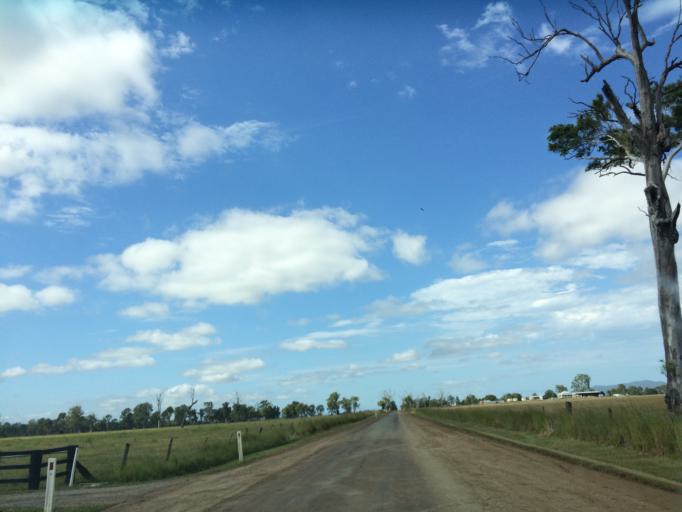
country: AU
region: Queensland
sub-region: Logan
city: Cedar Vale
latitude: -27.8730
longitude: 152.9566
